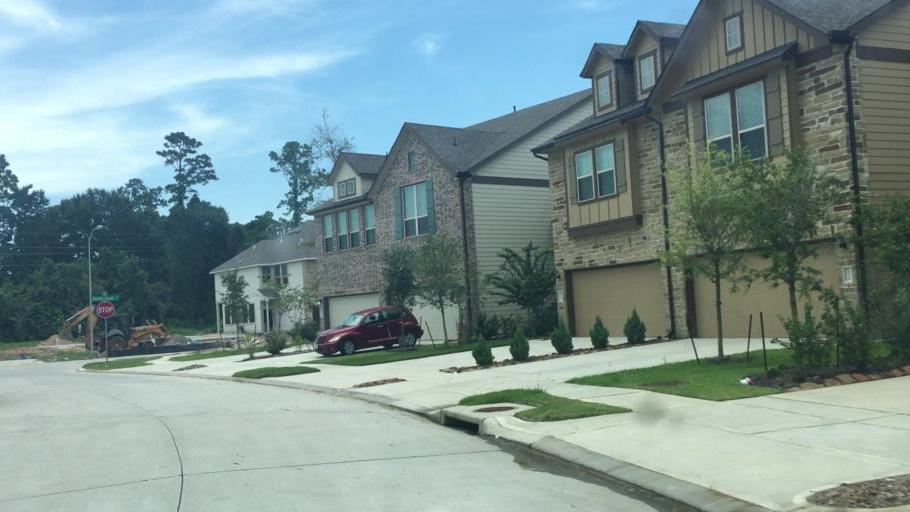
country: US
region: Texas
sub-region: Harris County
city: Atascocita
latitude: 29.9890
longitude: -95.1877
